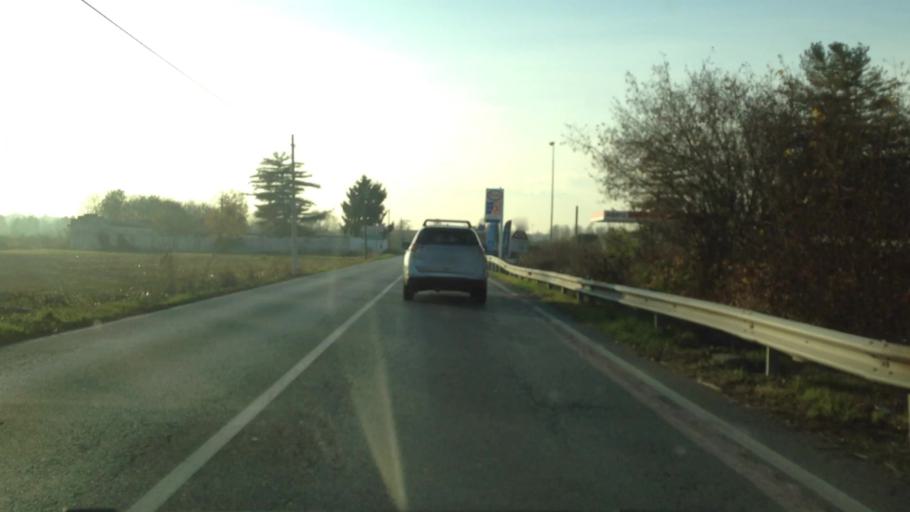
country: IT
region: Piedmont
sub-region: Provincia di Torino
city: Collegno
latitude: 45.0968
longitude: 7.5944
